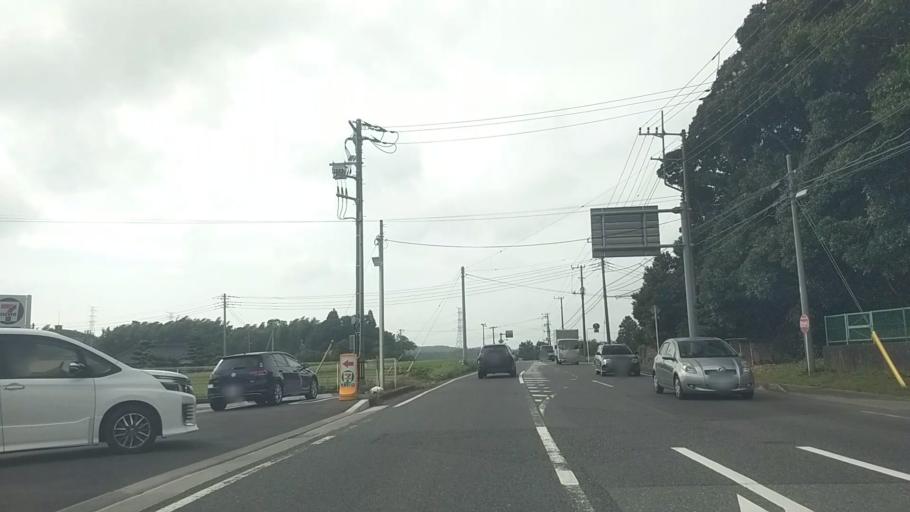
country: JP
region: Chiba
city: Kimitsu
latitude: 35.2778
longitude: 139.9917
